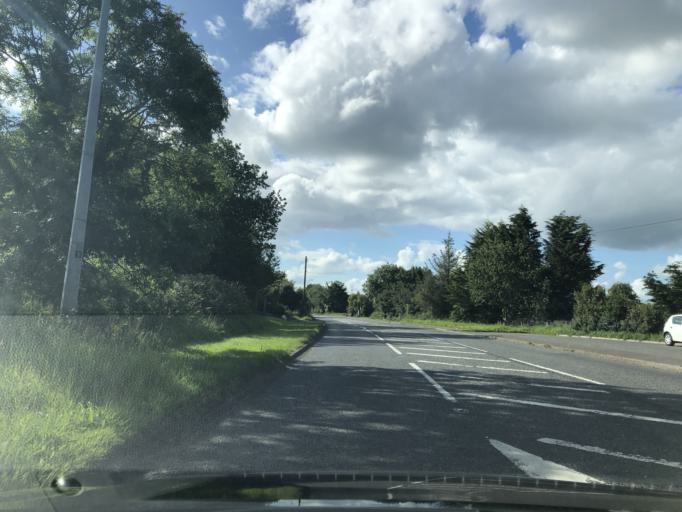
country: GB
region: Northern Ireland
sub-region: Ards District
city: Comber
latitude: 54.5680
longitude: -5.7691
